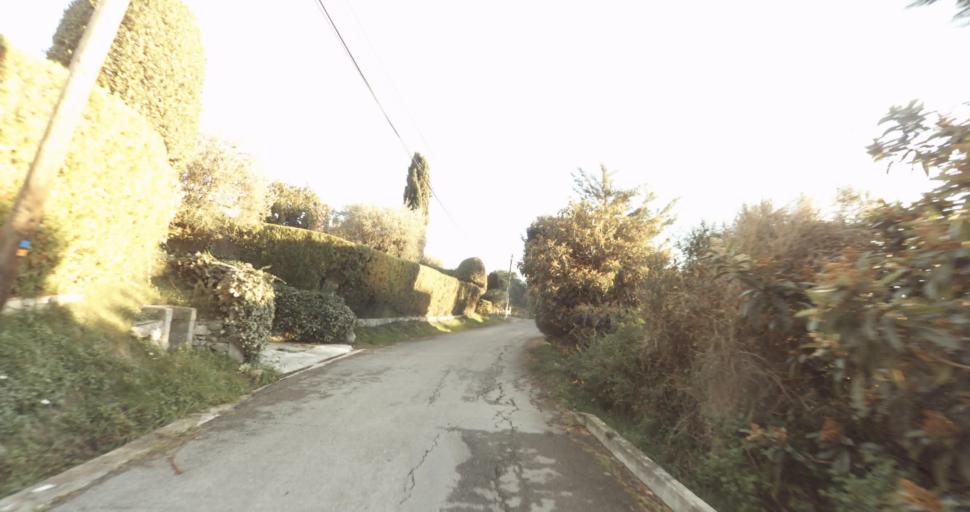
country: FR
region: Provence-Alpes-Cote d'Azur
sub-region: Departement des Alpes-Maritimes
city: Vence
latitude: 43.7301
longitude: 7.0899
